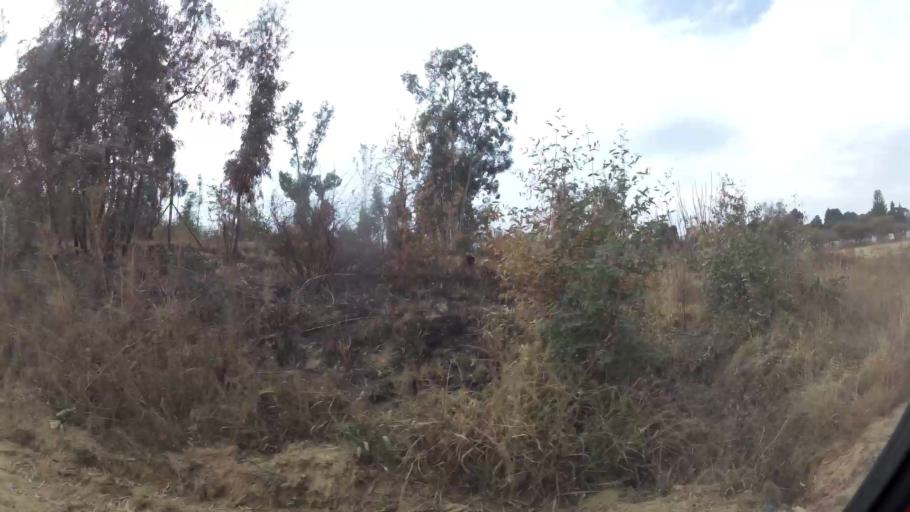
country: ZA
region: Gauteng
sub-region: West Rand District Municipality
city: Muldersdriseloop
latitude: -26.0660
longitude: 27.8939
